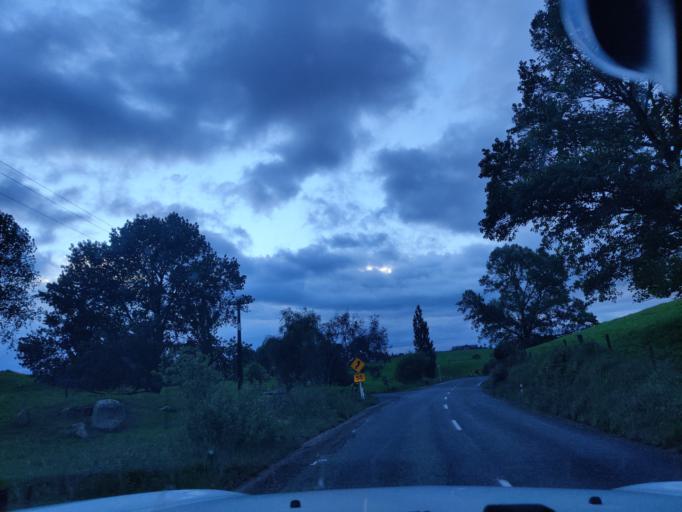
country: NZ
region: Waikato
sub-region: South Waikato District
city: Tokoroa
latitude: -38.1620
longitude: 175.7660
